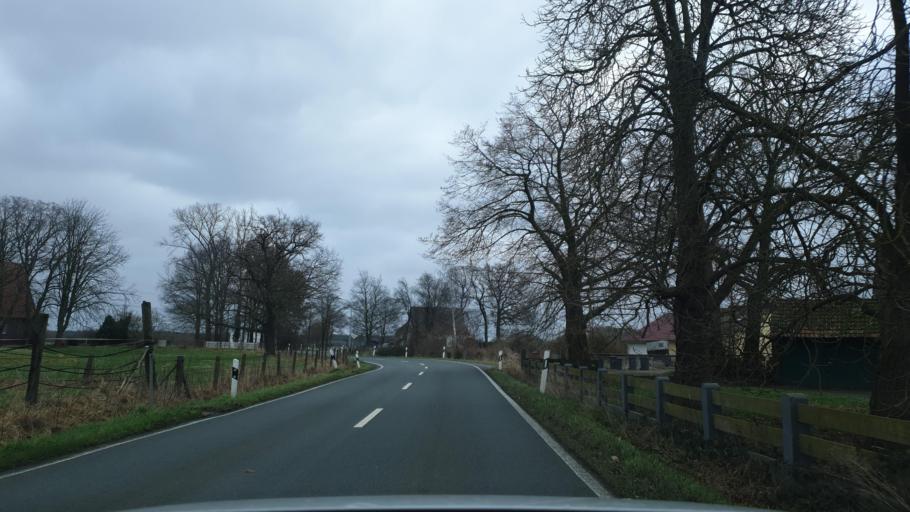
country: DE
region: North Rhine-Westphalia
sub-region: Regierungsbezirk Detmold
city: Petershagen
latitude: 52.3674
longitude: 8.8876
